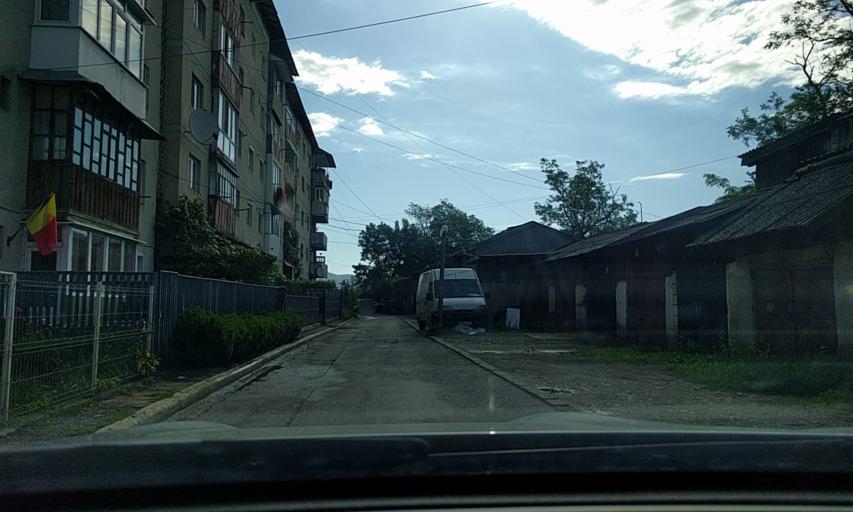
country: RO
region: Bistrita-Nasaud
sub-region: Oras Nasaud
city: Nasaud
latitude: 47.2818
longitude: 24.4155
